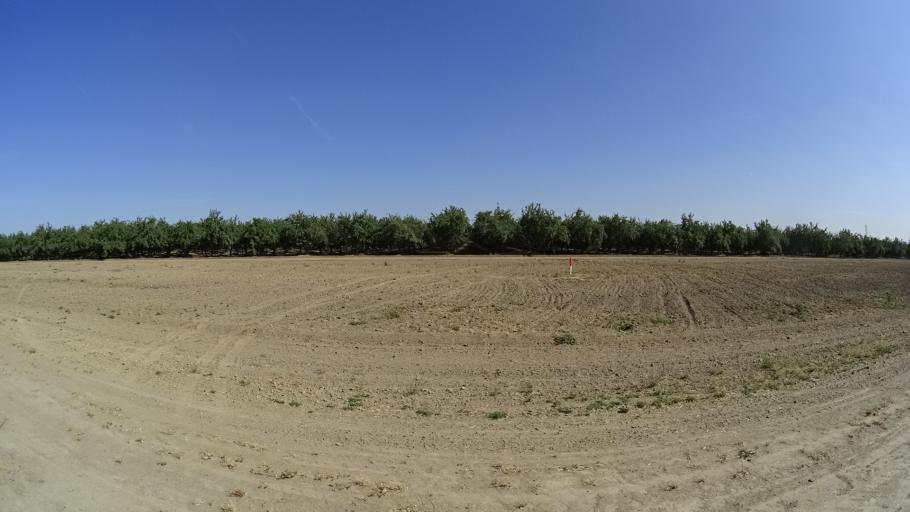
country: US
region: California
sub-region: Kings County
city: Home Garden
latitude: 36.2548
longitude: -119.5960
